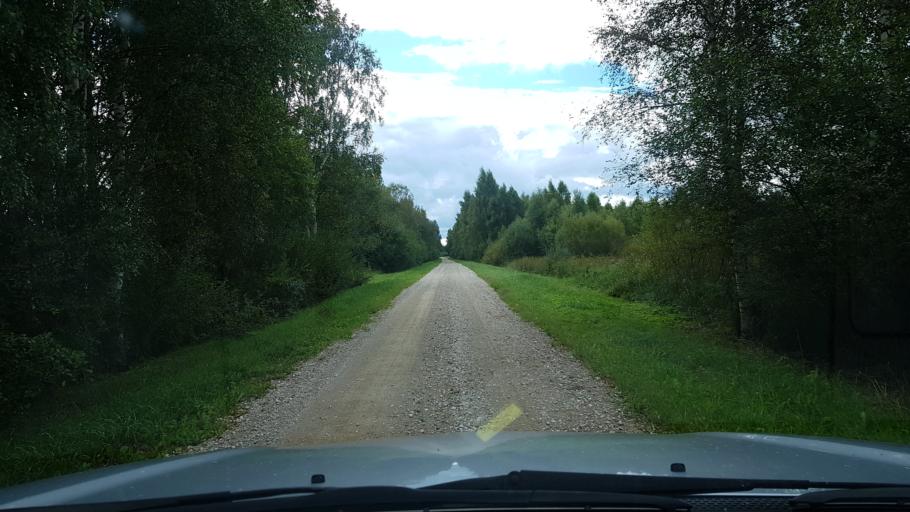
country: EE
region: Harju
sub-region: Rae vald
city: Vaida
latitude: 59.2789
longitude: 25.0503
